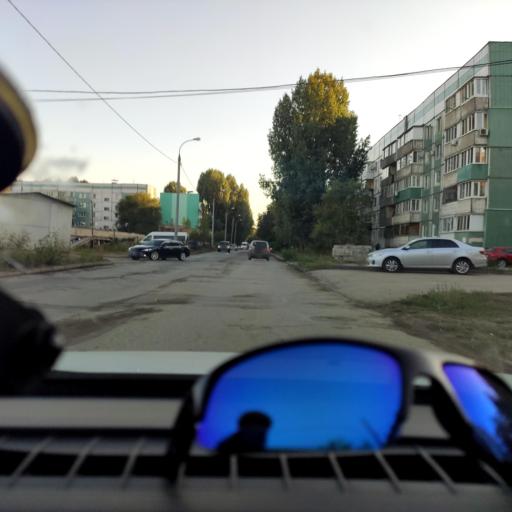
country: RU
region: Samara
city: Samara
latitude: 53.1231
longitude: 50.0957
